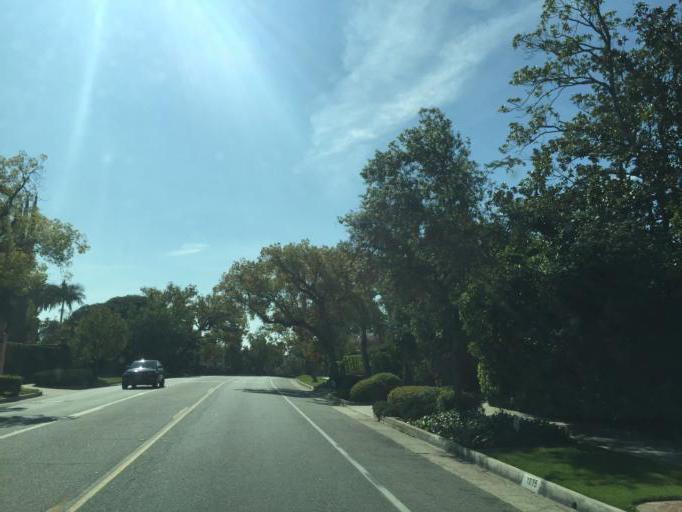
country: US
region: California
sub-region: Los Angeles County
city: South Pasadena
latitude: 34.1289
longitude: -118.1356
